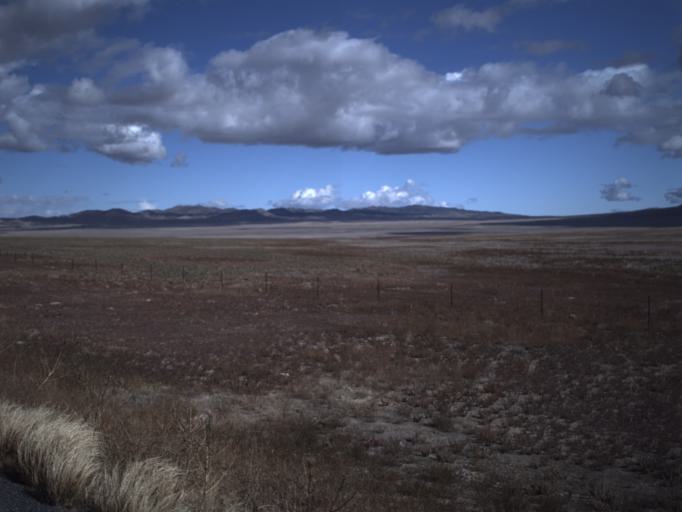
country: US
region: Utah
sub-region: Beaver County
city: Milford
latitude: 38.6373
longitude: -113.8589
